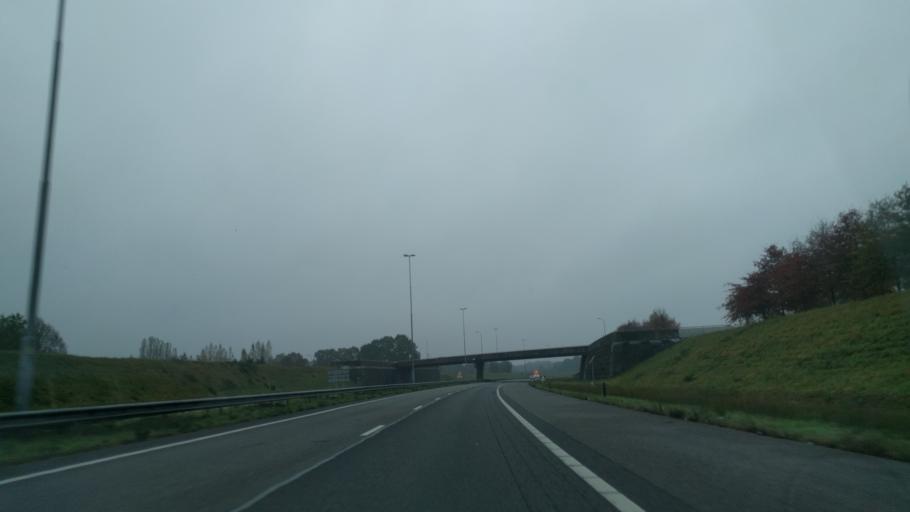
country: NL
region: North Brabant
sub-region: Gemeente Zundert
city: Zundert
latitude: 51.5612
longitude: 4.6565
